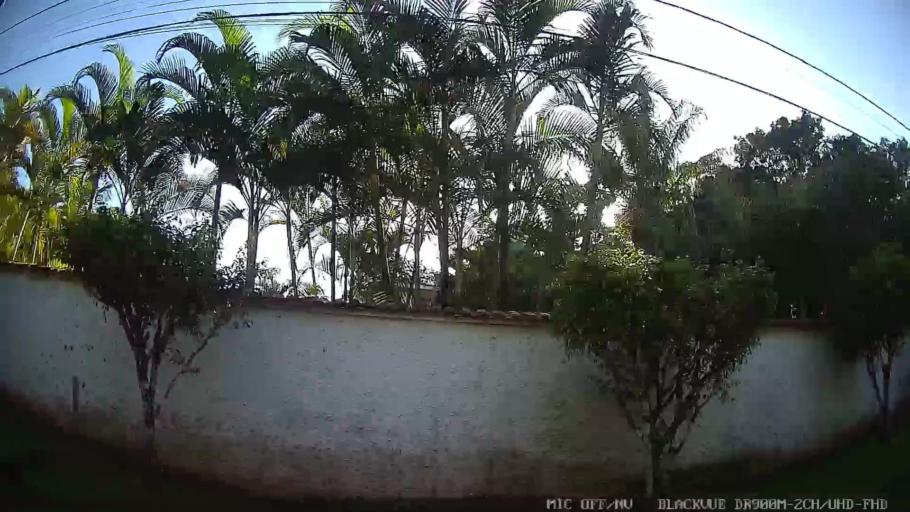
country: BR
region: Sao Paulo
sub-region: Itanhaem
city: Itanhaem
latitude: -24.2001
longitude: -46.8895
